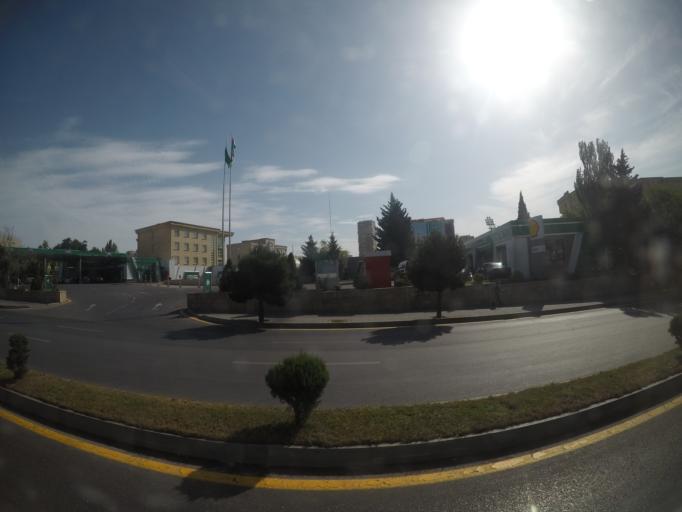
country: AZ
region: Baki
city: Badamdar
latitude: 40.3886
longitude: 49.8264
